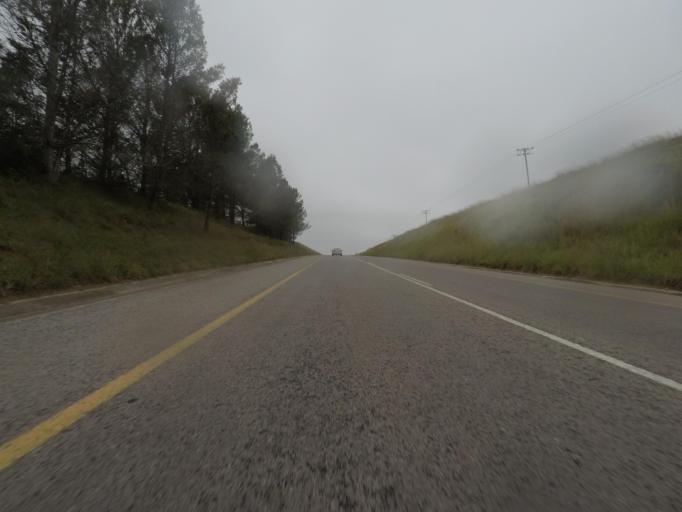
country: ZA
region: Eastern Cape
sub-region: Cacadu District Municipality
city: Grahamstown
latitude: -33.6452
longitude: 26.3791
